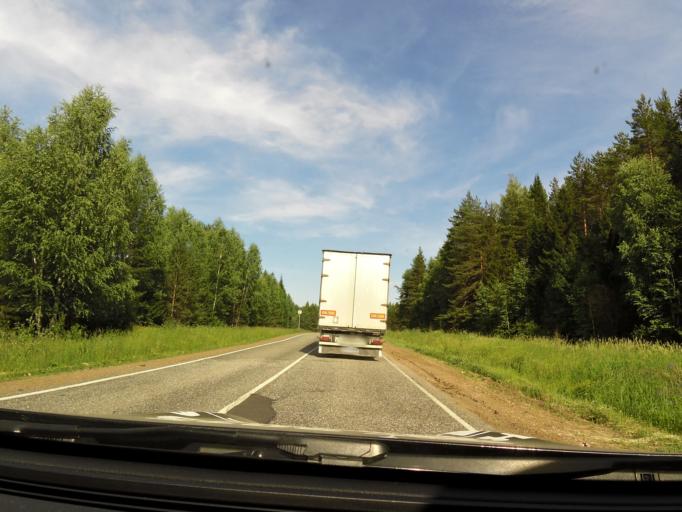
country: RU
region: Kirov
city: Belaya Kholunitsa
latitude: 58.8079
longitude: 50.5620
